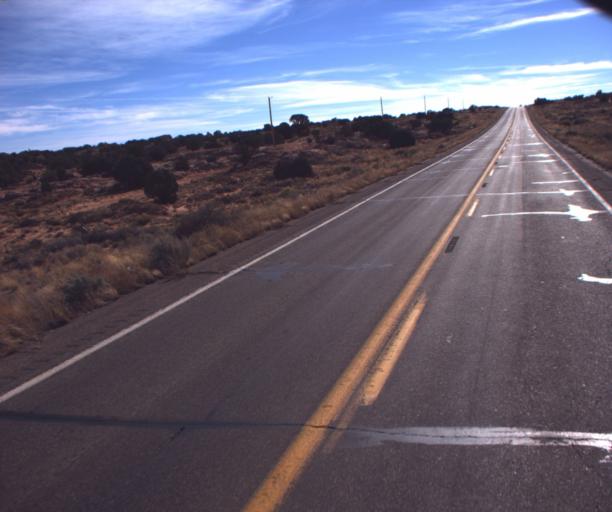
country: US
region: Arizona
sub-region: Coconino County
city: Kaibito
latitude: 36.6009
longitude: -111.1714
